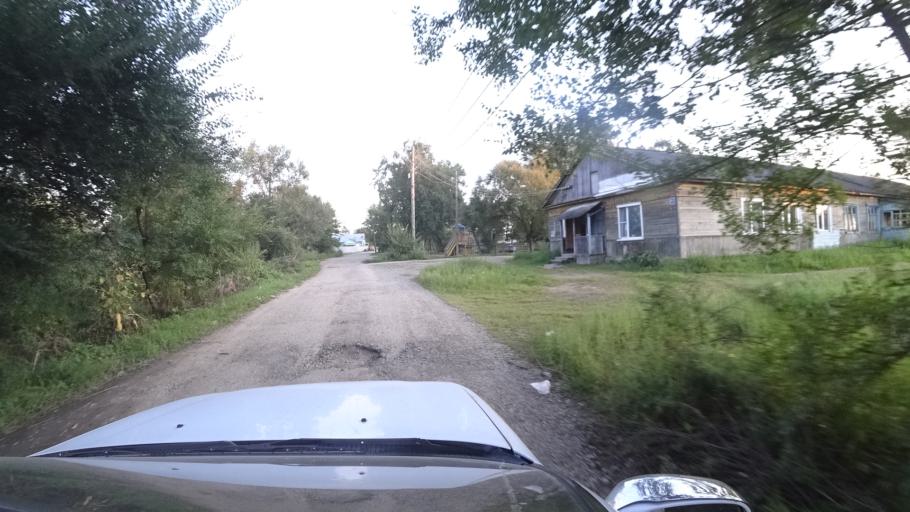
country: RU
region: Primorskiy
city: Dal'nerechensk
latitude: 45.9452
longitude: 133.7554
